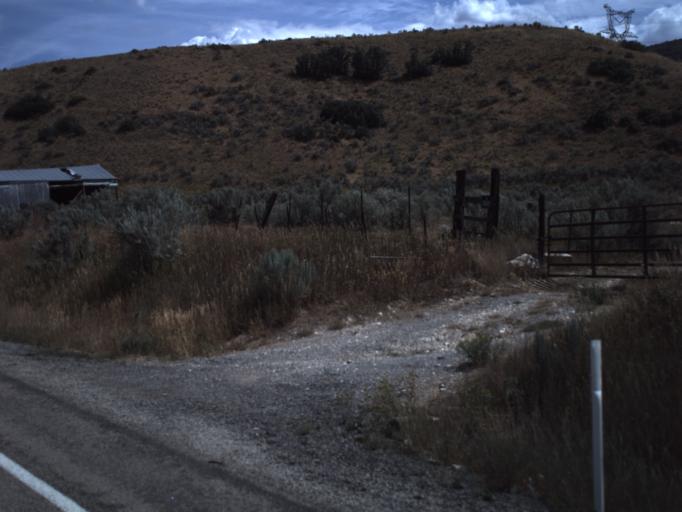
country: US
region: Utah
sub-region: Utah County
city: Woodland Hills
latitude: 39.9698
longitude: -111.5089
